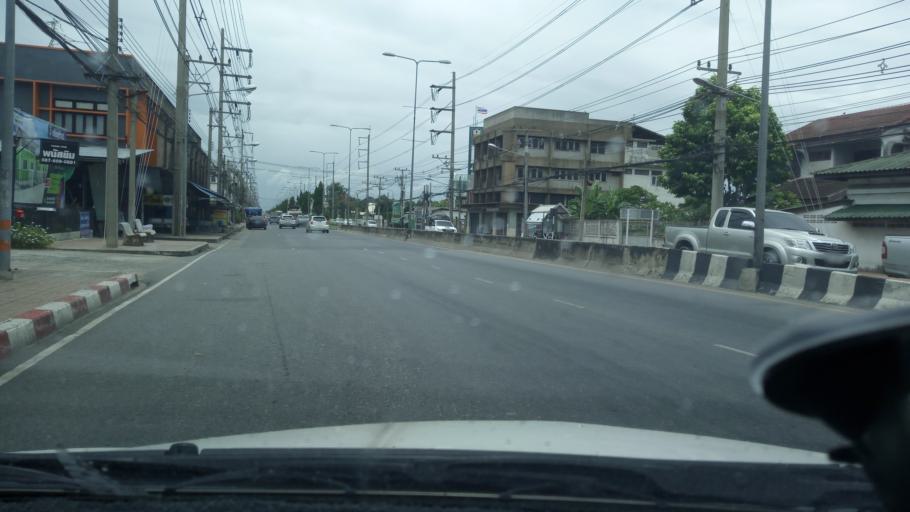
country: TH
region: Chon Buri
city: Phanat Nikhom
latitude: 13.4507
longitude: 101.1757
